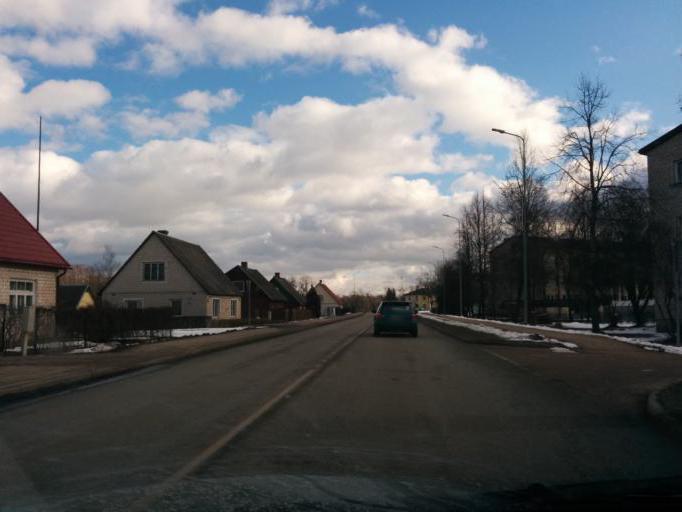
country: LV
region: Balvu Rajons
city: Balvi
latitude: 57.1400
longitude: 27.2493
